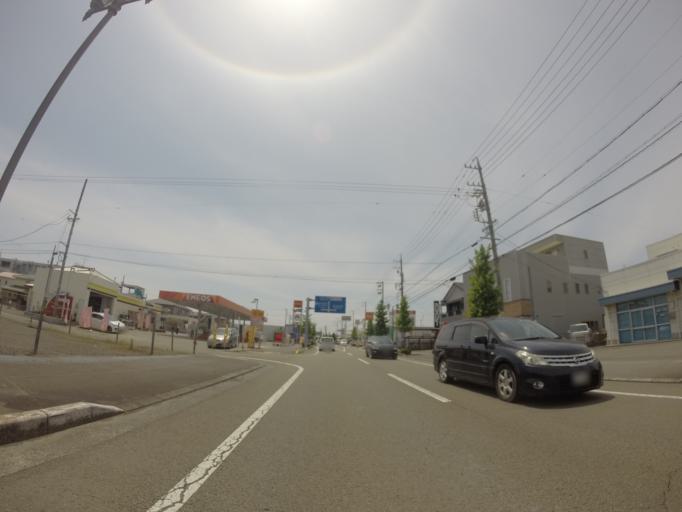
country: JP
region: Shizuoka
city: Yaizu
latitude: 34.8439
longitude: 138.3080
